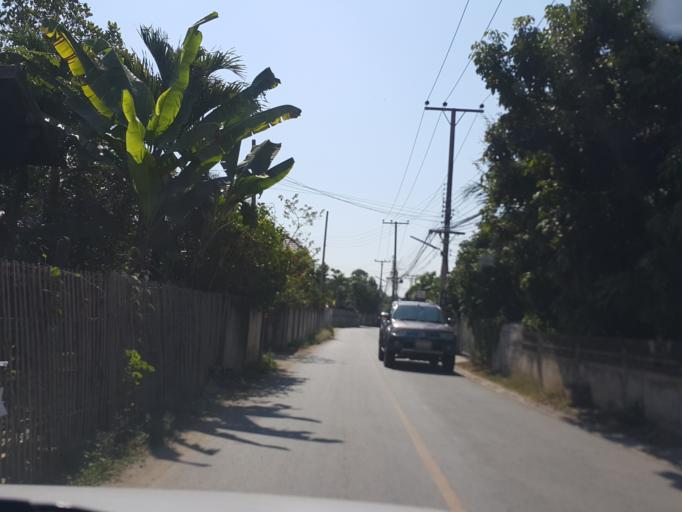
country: TH
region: Chiang Mai
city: San Kamphaeng
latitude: 18.7440
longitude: 99.1132
